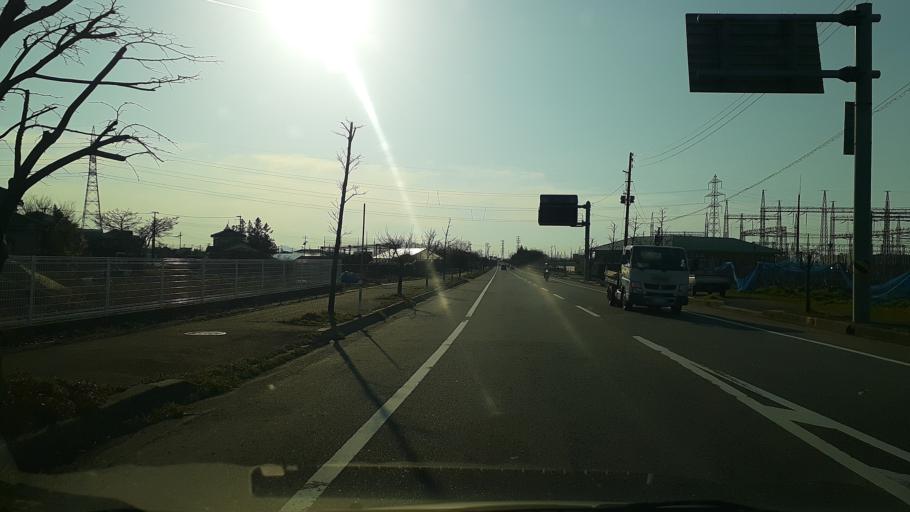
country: JP
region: Niigata
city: Niitsu-honcho
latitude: 37.8065
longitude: 139.1440
